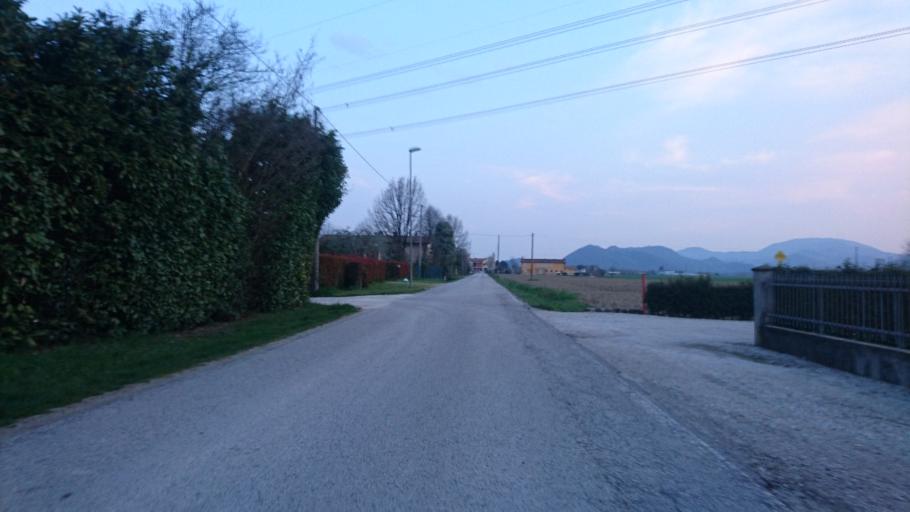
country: IT
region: Veneto
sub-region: Provincia di Padova
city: Saccolongo
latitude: 45.3989
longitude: 11.7313
